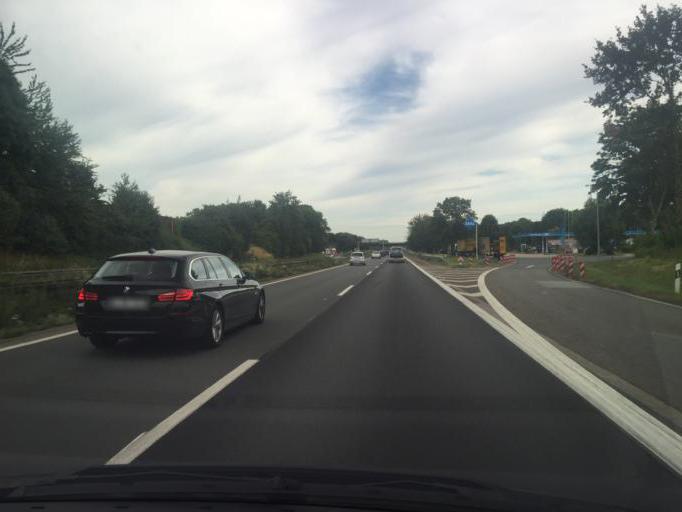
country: DE
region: North Rhine-Westphalia
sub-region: Regierungsbezirk Dusseldorf
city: Krefeld
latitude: 51.3087
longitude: 6.6347
